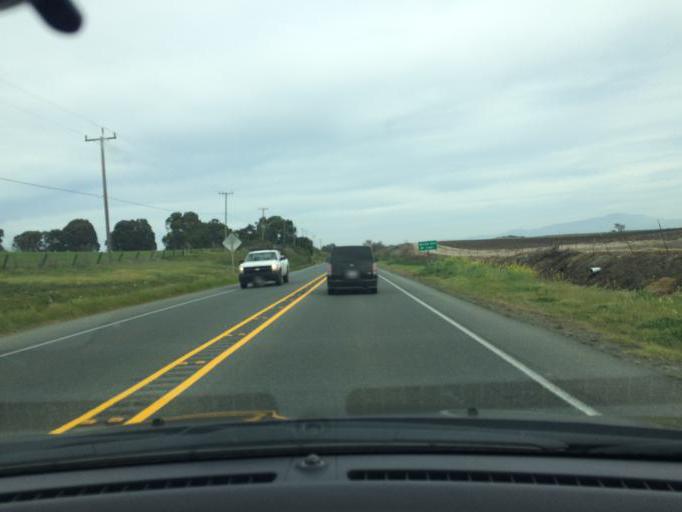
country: US
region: California
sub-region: Monterey County
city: Castroville
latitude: 36.7704
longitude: -121.7365
